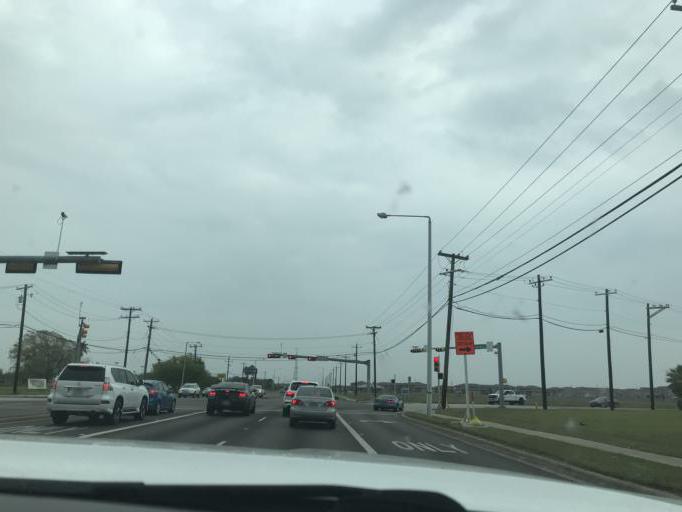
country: US
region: Texas
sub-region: Nueces County
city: Corpus Christi
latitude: 27.6760
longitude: -97.3648
